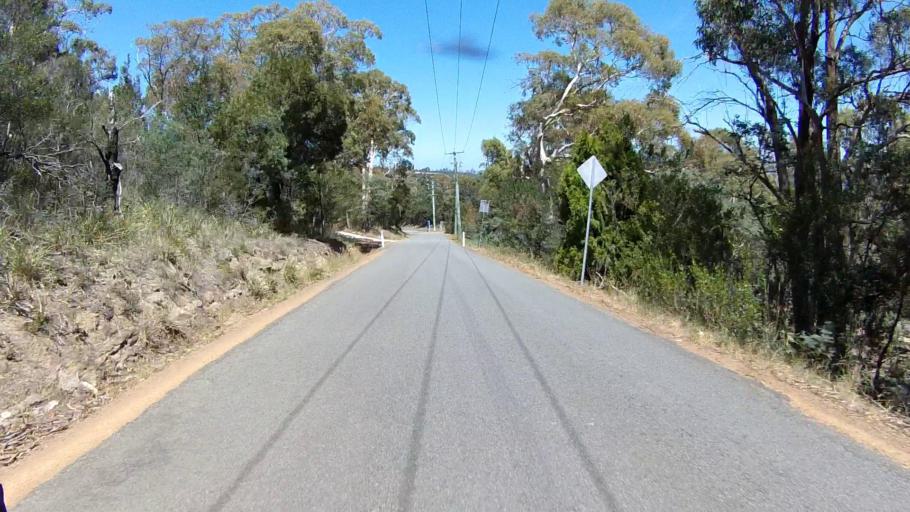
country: AU
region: Tasmania
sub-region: Clarence
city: Cambridge
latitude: -42.8549
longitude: 147.4217
